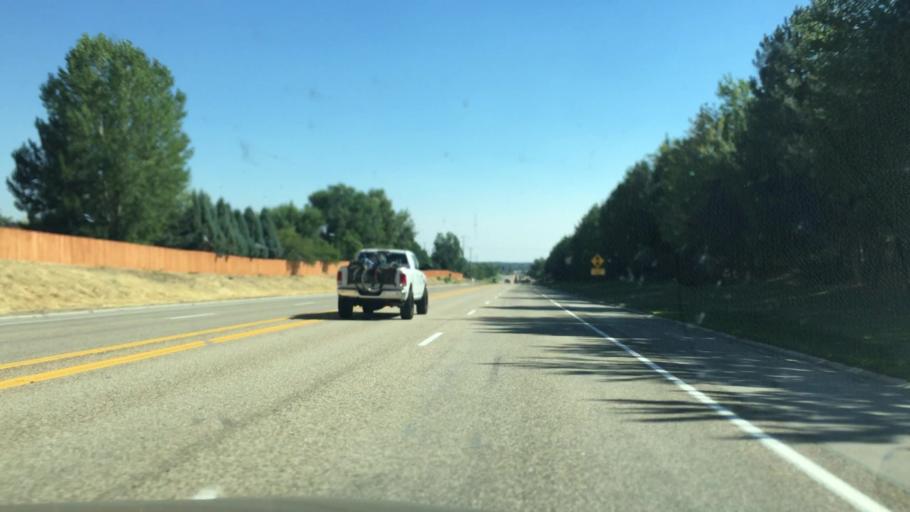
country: US
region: Idaho
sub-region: Ada County
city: Eagle
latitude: 43.7103
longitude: -116.3189
